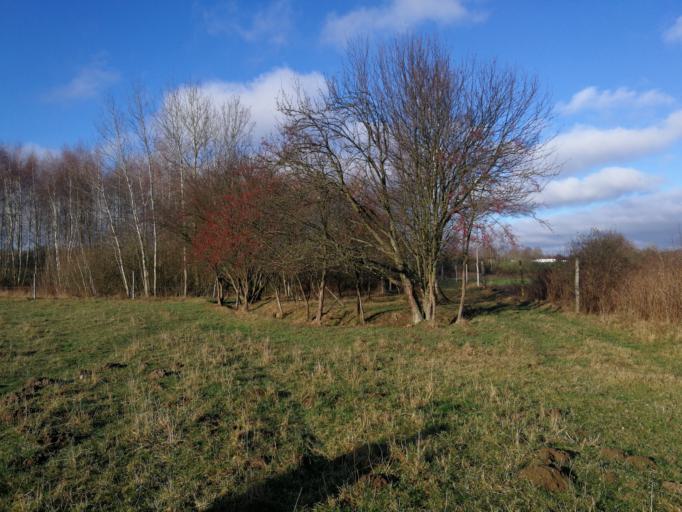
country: PL
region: Warmian-Masurian Voivodeship
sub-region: Powiat dzialdowski
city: Rybno
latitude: 53.4149
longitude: 19.9145
